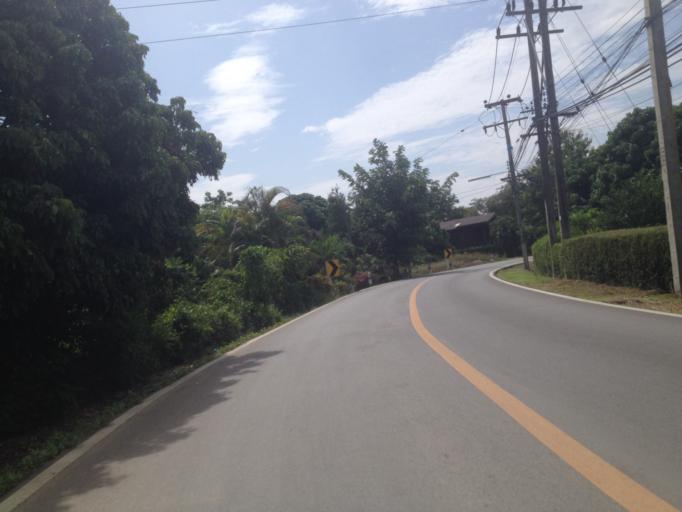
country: TH
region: Chiang Mai
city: Hang Dong
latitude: 18.6785
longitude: 98.9816
